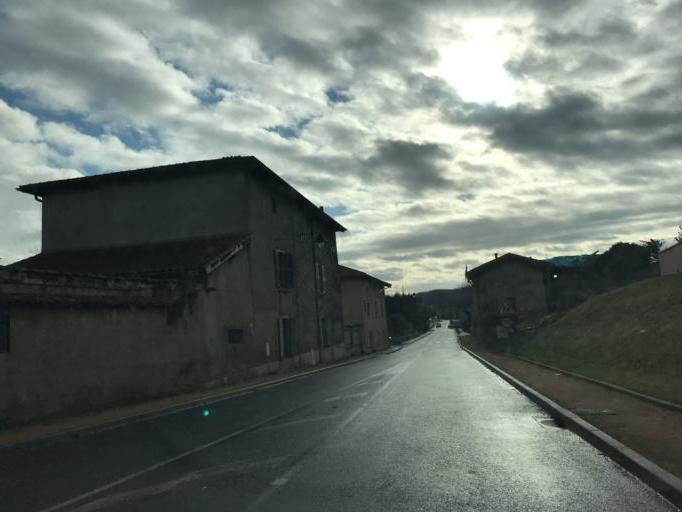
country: FR
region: Rhone-Alpes
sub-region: Departement de l'Ain
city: Sainte-Euphemie
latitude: 45.9742
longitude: 4.7989
